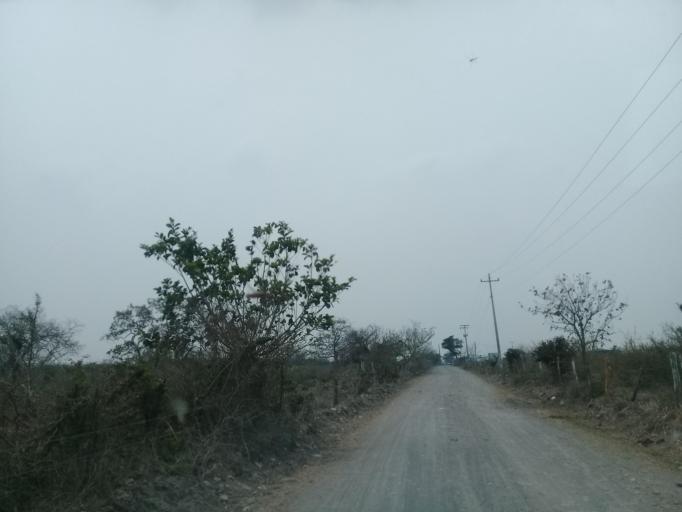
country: MX
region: Veracruz
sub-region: Medellin
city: La Laguna y Monte del Castillo
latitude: 18.9046
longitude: -96.1254
